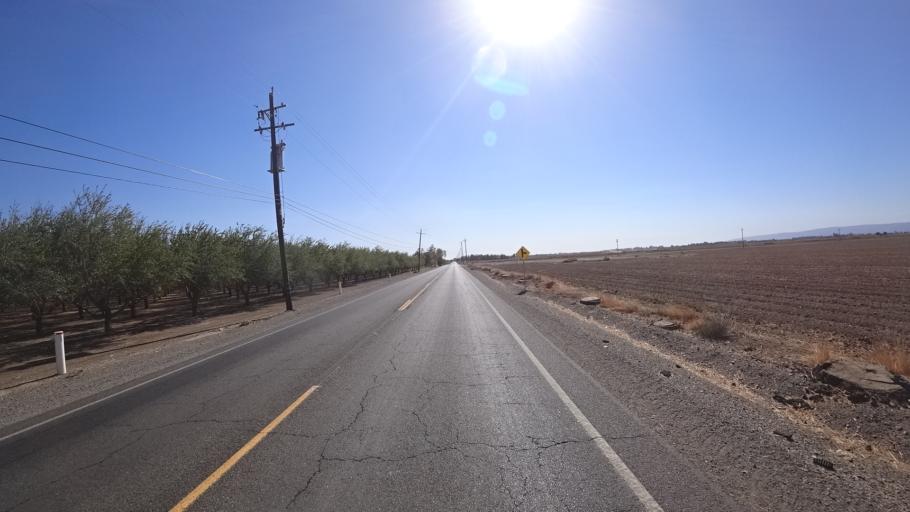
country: US
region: California
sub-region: Yolo County
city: Davis
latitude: 38.5778
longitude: -121.8032
